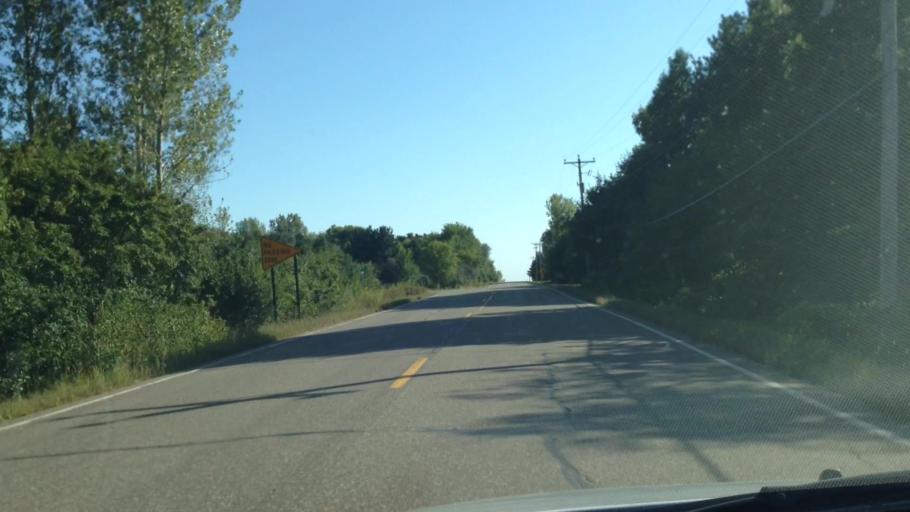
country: US
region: Minnesota
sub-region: Washington County
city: Stillwater
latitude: 45.0906
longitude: -92.8128
